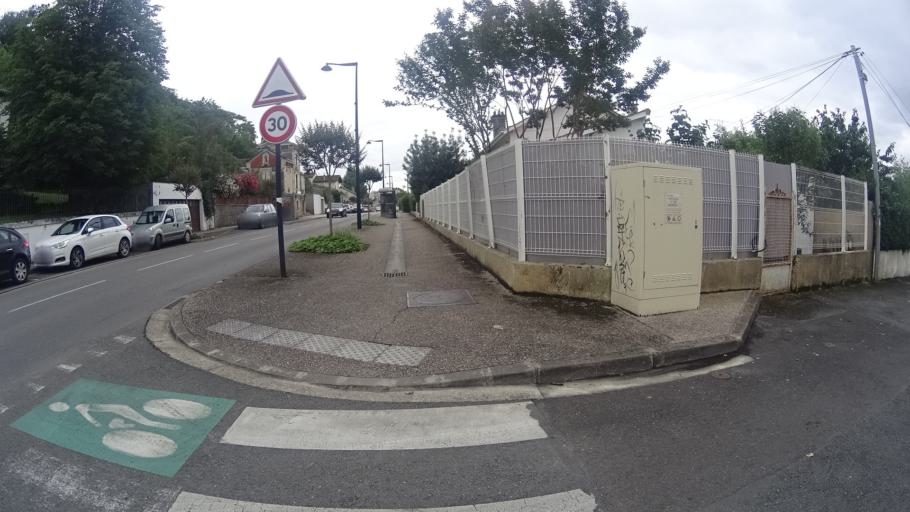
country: FR
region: Aquitaine
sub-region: Departement de la Gironde
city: Floirac
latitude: 44.8353
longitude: -0.5301
